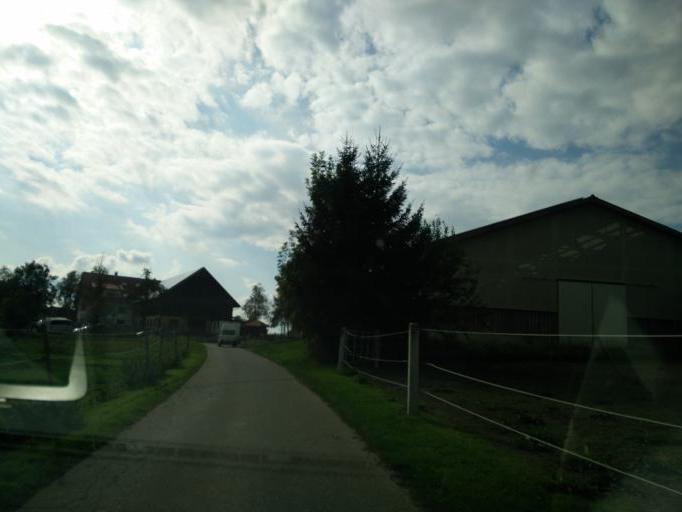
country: DE
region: Baden-Wuerttemberg
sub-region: Tuebingen Region
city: Kisslegg
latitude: 47.8169
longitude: 9.8724
